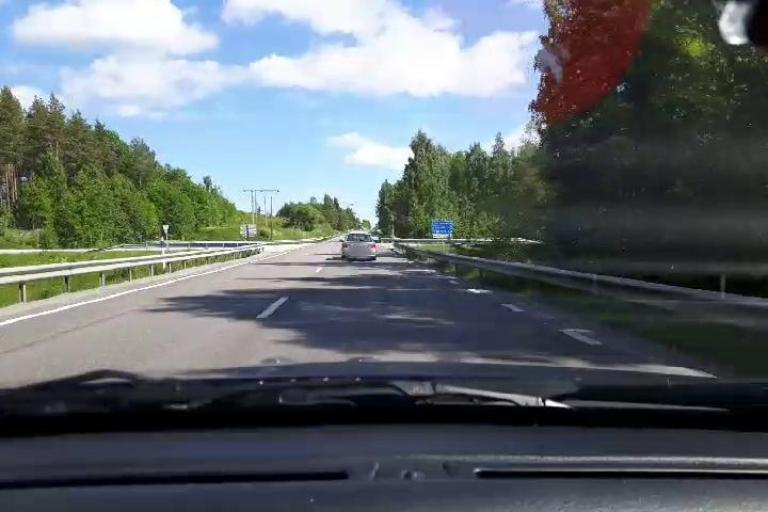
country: SE
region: Gaevleborg
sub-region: Hudiksvalls Kommun
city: Sorforsa
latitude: 61.7363
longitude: 16.9248
